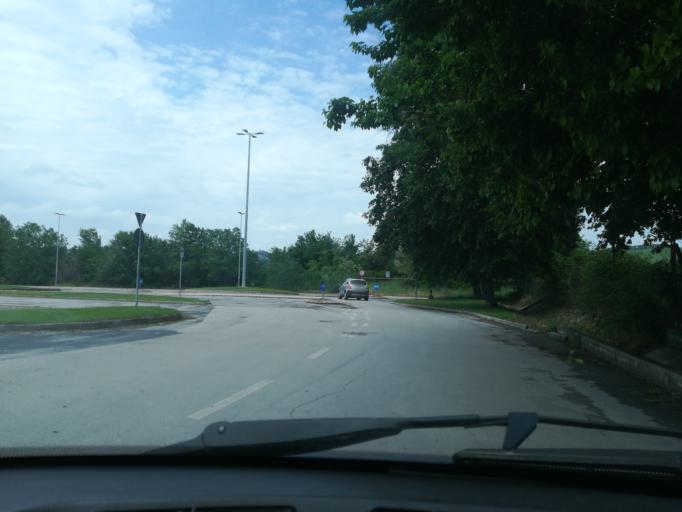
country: IT
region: The Marches
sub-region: Provincia di Macerata
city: Piediripa
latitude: 43.2813
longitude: 13.5033
